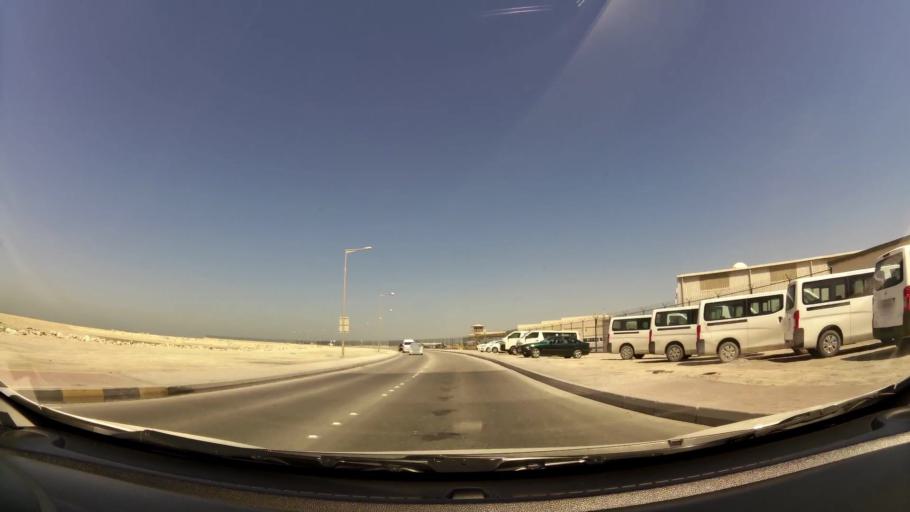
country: BH
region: Muharraq
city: Al Muharraq
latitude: 26.2783
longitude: 50.6129
